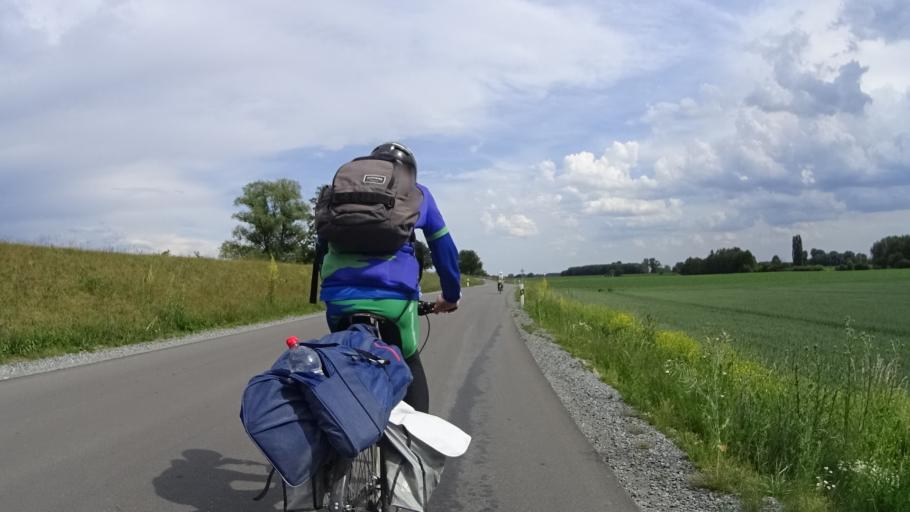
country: DE
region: Bavaria
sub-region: Upper Palatinate
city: Worth an der Donau
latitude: 48.9923
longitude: 12.4018
